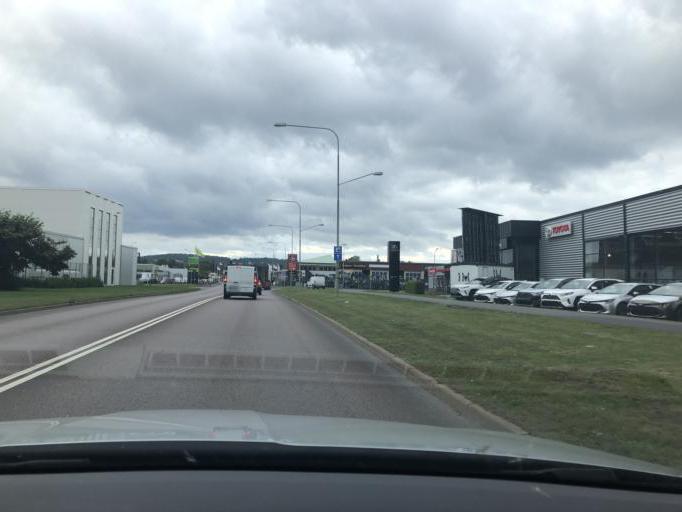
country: SE
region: Joenkoeping
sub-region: Jonkopings Kommun
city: Jonkoping
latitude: 57.7655
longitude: 14.1799
